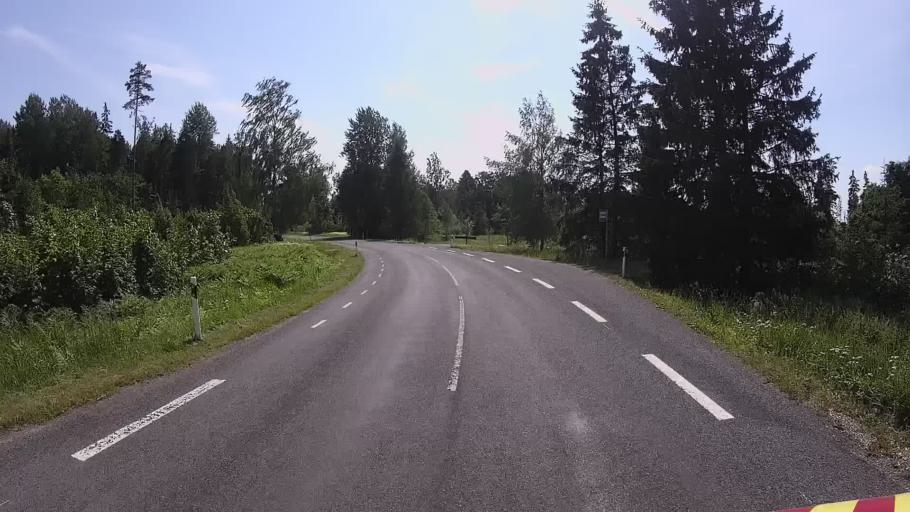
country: EE
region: Viljandimaa
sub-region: Karksi vald
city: Karksi-Nuia
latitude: 58.0314
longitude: 25.5418
